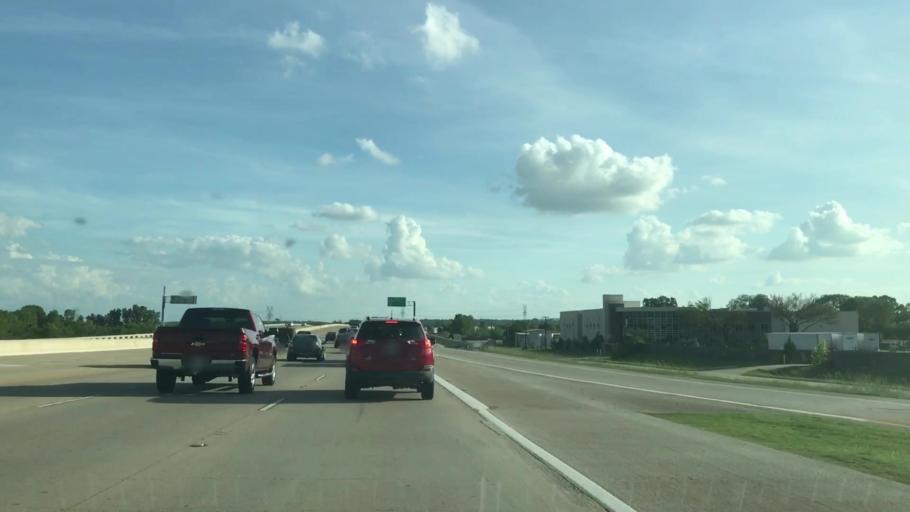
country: US
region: Texas
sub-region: Dallas County
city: Grand Prairie
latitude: 32.7972
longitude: -97.0189
